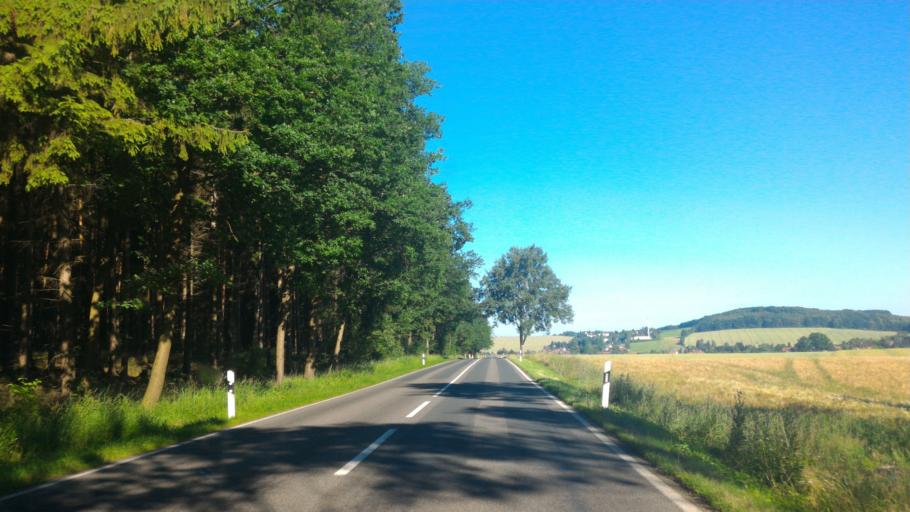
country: DE
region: Saxony
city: Hainewalde
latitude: 50.9323
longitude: 14.7043
